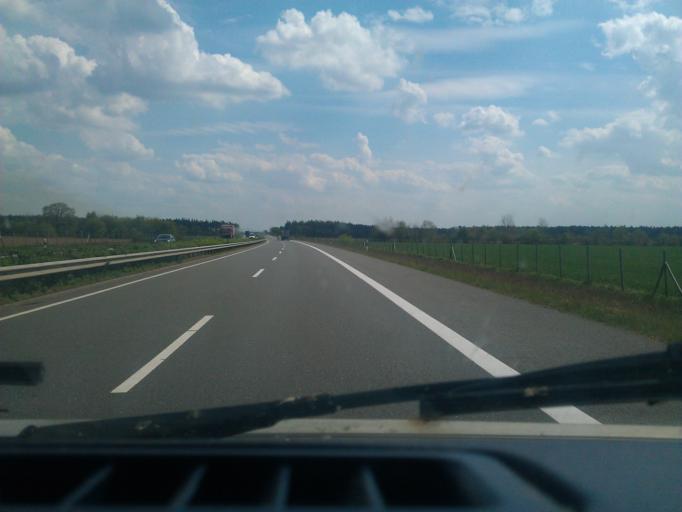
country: DE
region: Lower Saxony
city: Emsburen
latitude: 52.3780
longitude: 7.2472
